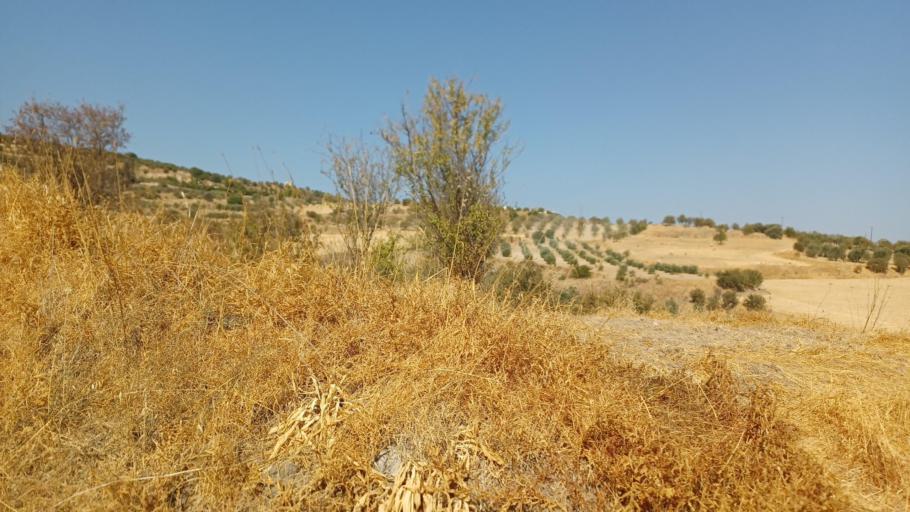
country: CY
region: Pafos
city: Polis
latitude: 34.9486
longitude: 32.5142
